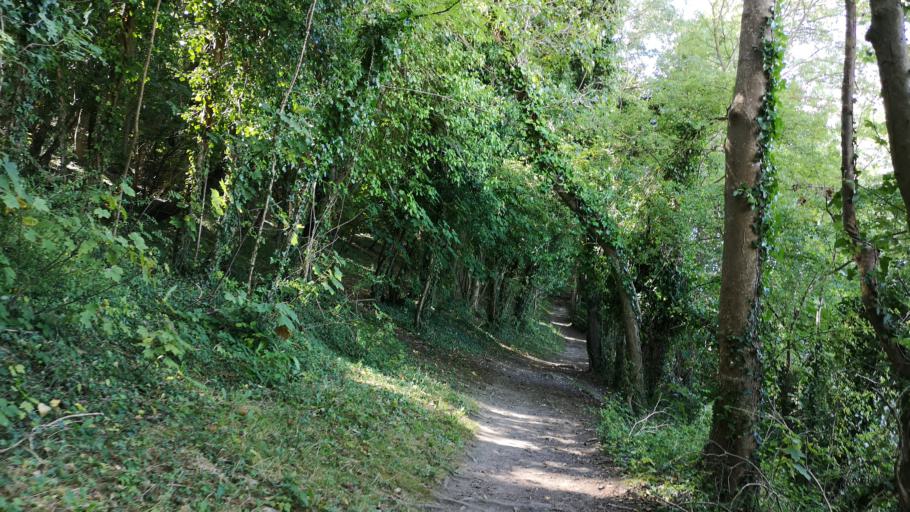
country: GB
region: England
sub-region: Isle of Wight
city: Totland
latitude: 50.6701
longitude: -1.5351
